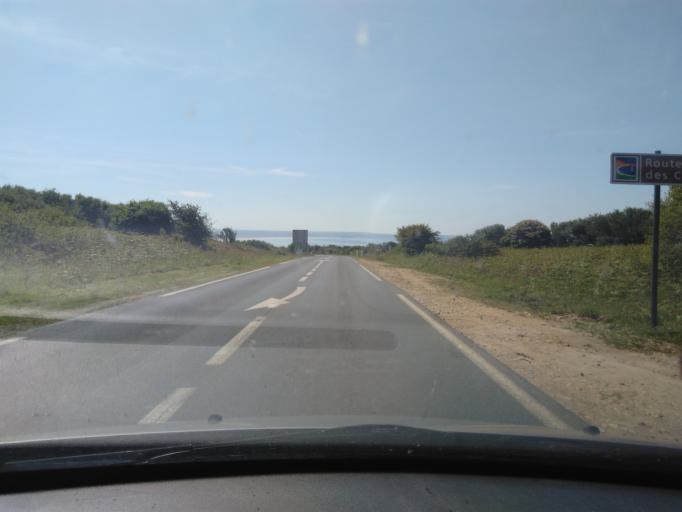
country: FR
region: Lower Normandy
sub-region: Departement de la Manche
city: Beaumont-Hague
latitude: 49.6802
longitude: -1.9010
